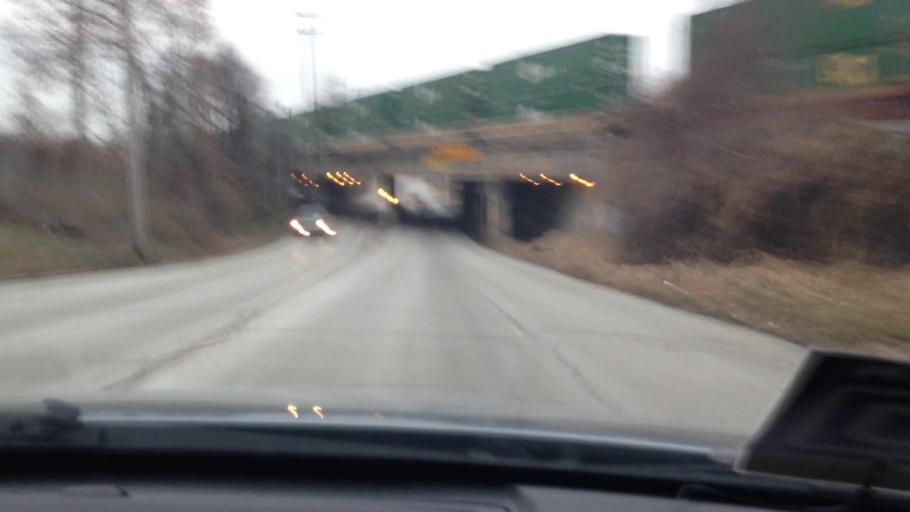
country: US
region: Missouri
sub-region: Clay County
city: North Kansas City
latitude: 39.0981
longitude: -94.5285
